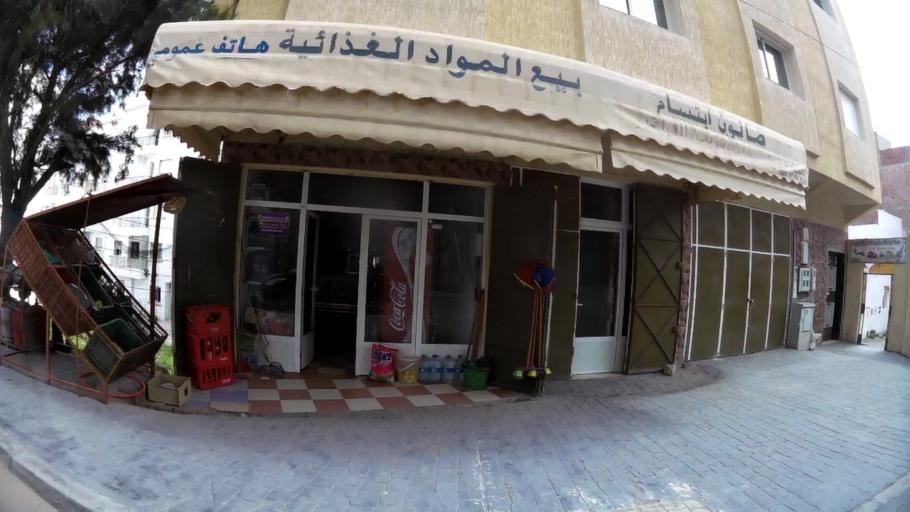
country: MA
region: Tanger-Tetouan
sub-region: Tanger-Assilah
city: Tangier
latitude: 35.7664
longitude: -5.7602
